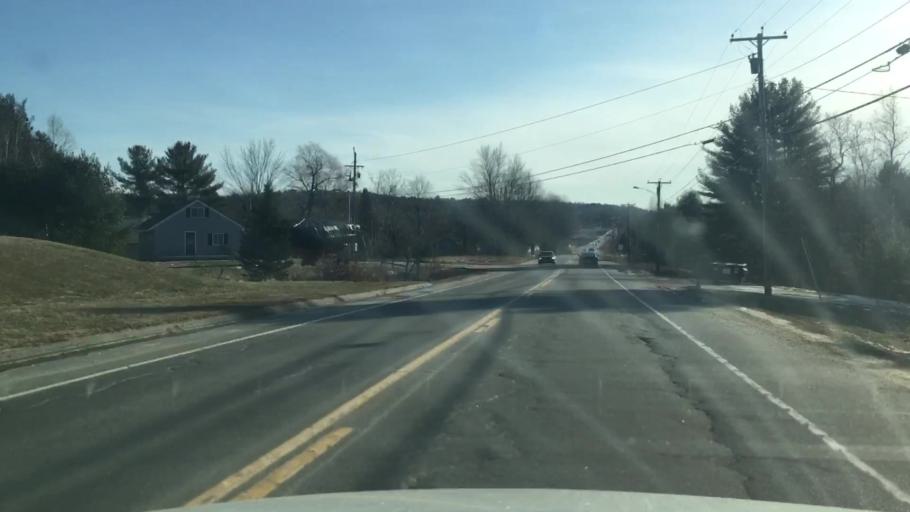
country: US
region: Maine
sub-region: Androscoggin County
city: Sabattus
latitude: 44.1087
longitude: -70.0894
